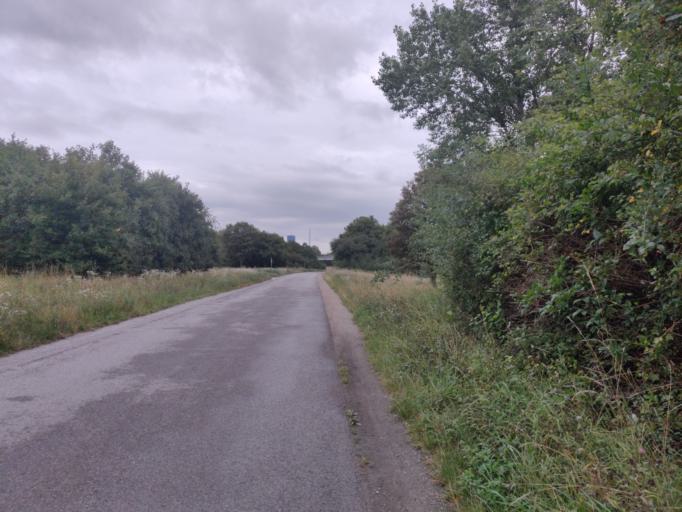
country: AT
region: Vienna
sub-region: Wien Stadt
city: Vienna
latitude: 48.2568
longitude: 16.3785
